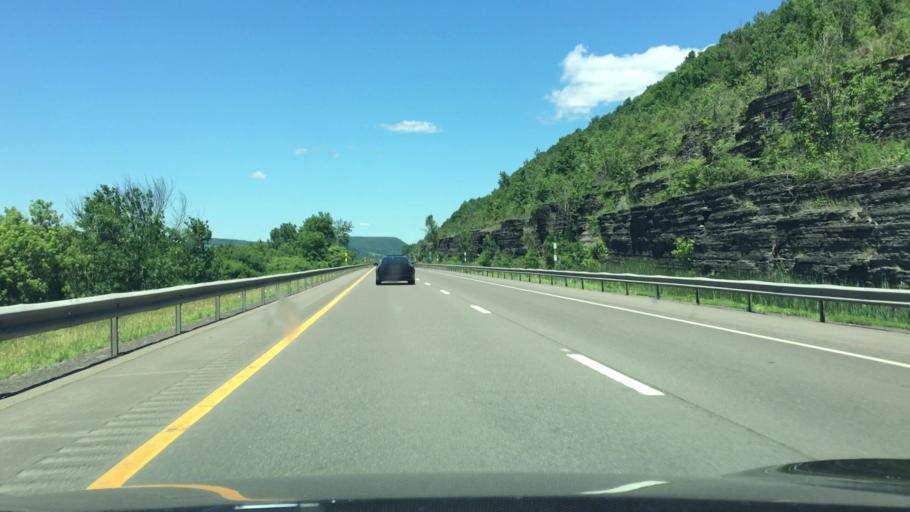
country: US
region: New York
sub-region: Cortland County
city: Homer
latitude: 42.6423
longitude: -76.1737
